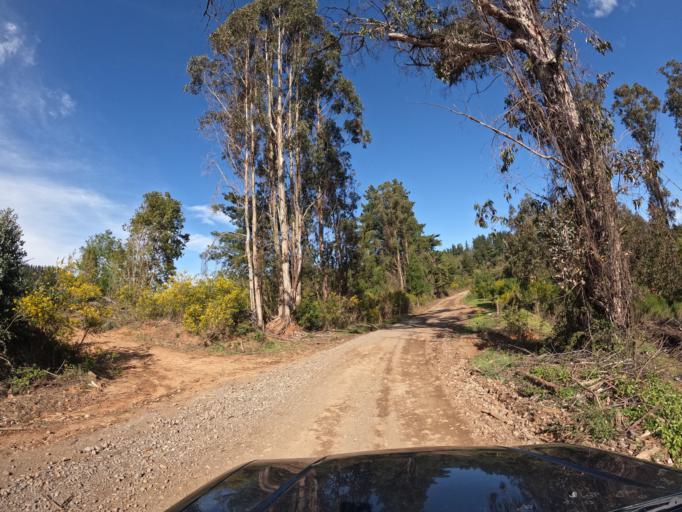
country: CL
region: Biobio
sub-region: Provincia de Biobio
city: La Laja
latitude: -37.0871
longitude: -72.8294
